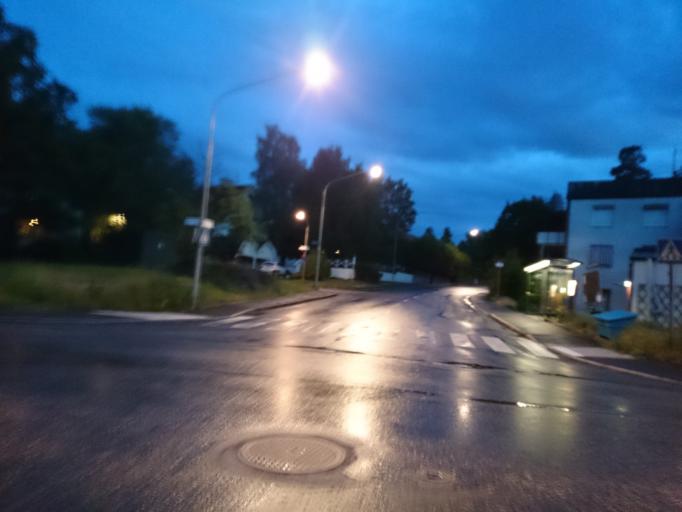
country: SE
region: Stockholm
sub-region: Stockholms Kommun
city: Arsta
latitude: 59.2869
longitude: 18.0274
